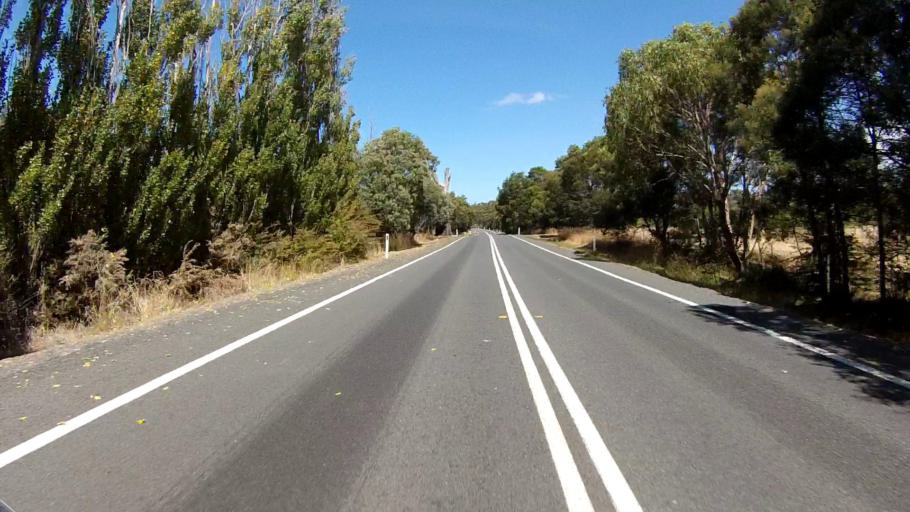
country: AU
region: Tasmania
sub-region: Break O'Day
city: St Helens
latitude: -42.0738
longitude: 148.0671
